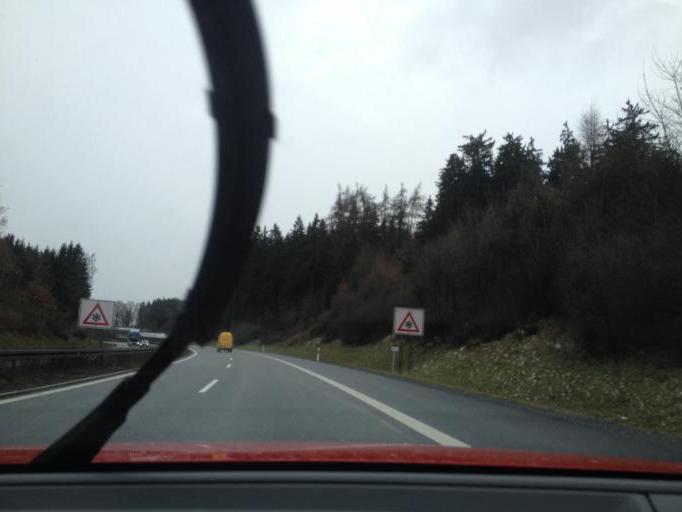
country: DE
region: Bavaria
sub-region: Upper Franconia
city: Schonwald
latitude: 50.1936
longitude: 12.1005
